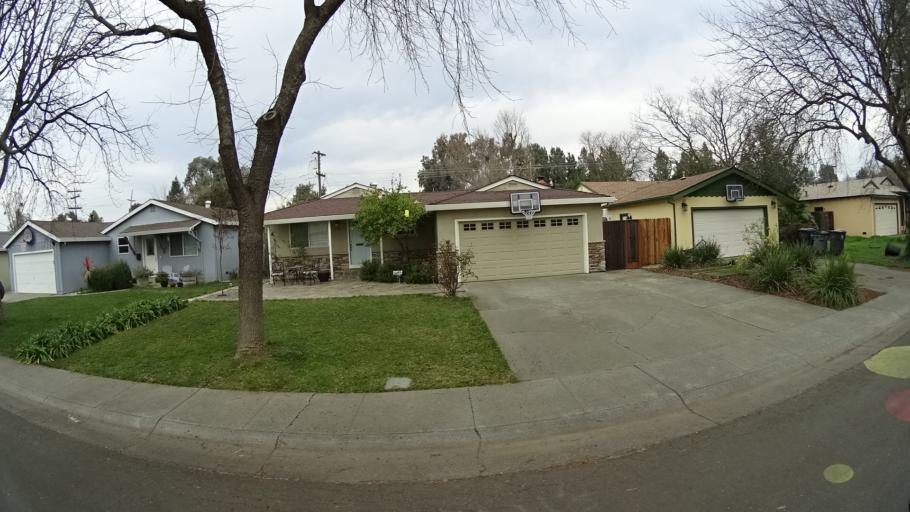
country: US
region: California
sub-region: Yolo County
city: Davis
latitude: 38.5616
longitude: -121.7292
